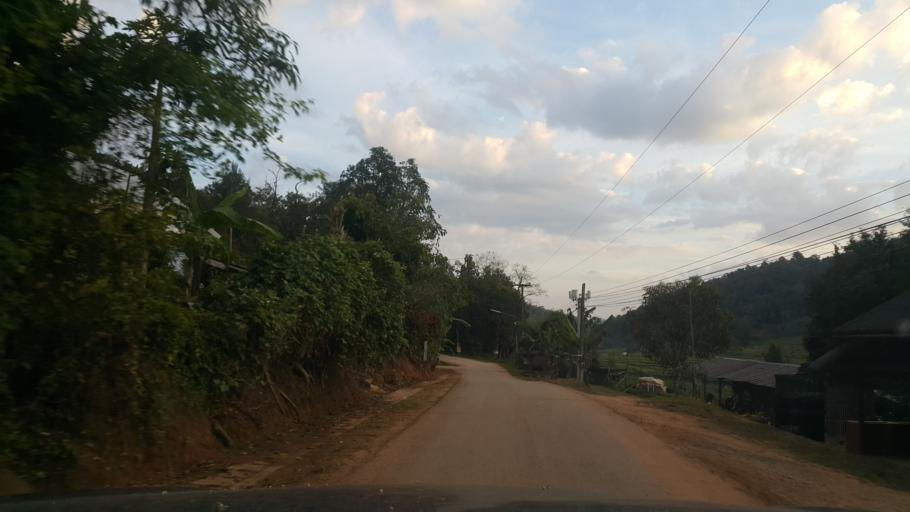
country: TH
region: Chiang Mai
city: Samoeng
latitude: 18.9774
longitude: 98.6777
